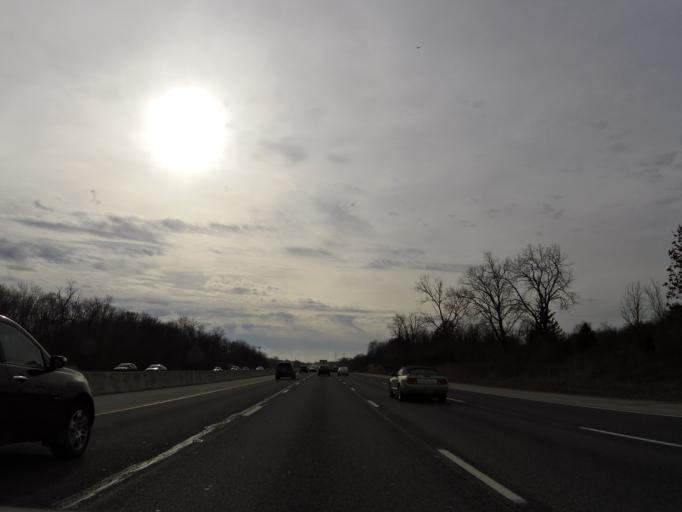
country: US
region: Indiana
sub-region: Marion County
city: Lawrence
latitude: 39.8743
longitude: -86.0475
